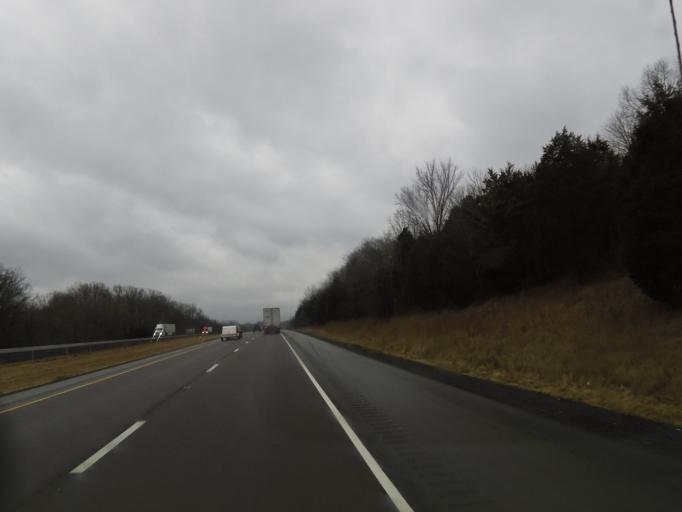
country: US
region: Illinois
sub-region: Williamson County
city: Marion
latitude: 37.6866
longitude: -88.9662
